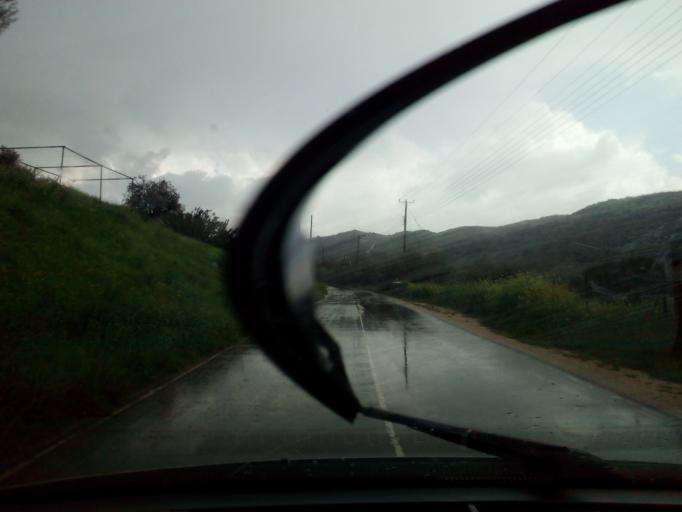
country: CY
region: Pafos
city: Polis
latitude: 34.9799
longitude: 32.4617
